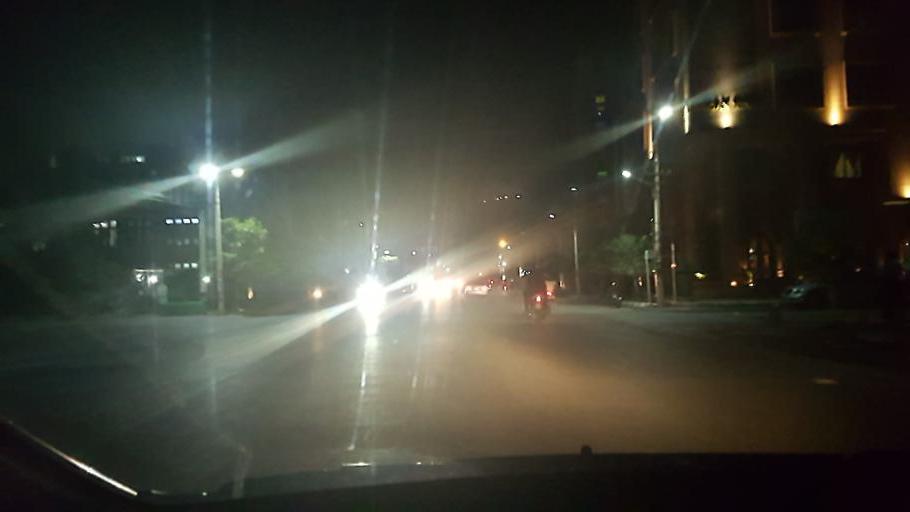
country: MM
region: Mandalay
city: Mandalay
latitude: 21.9792
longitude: 96.0957
